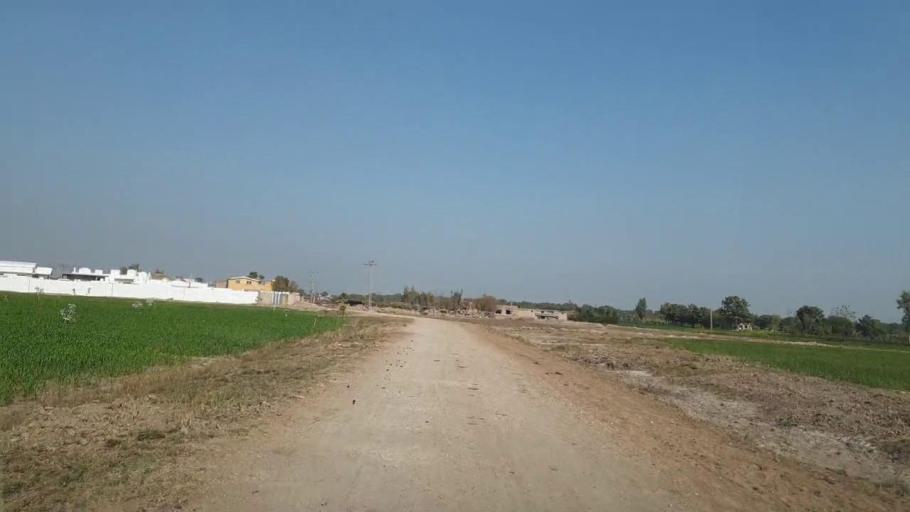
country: PK
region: Sindh
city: Matiari
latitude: 25.5057
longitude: 68.4588
